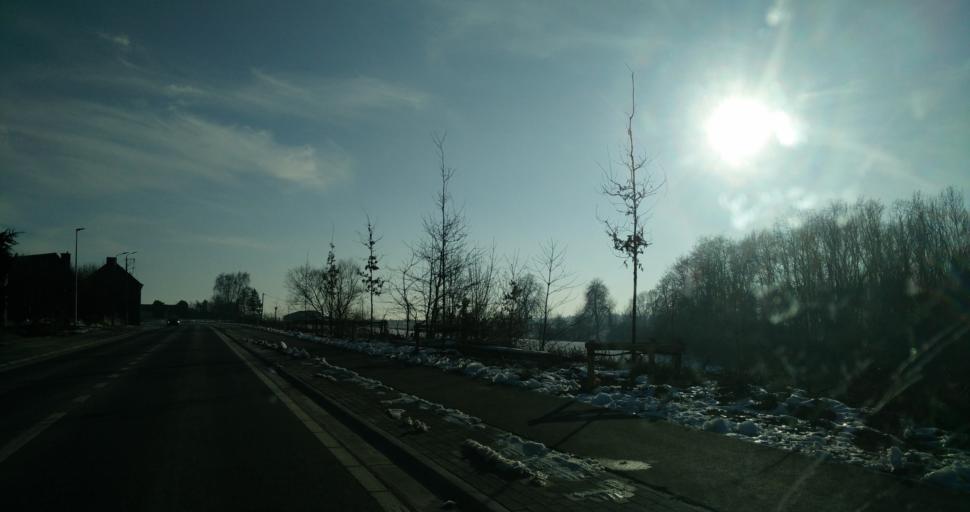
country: BE
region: Flanders
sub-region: Provincie Vlaams-Brabant
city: Halle
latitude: 50.7105
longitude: 4.2582
